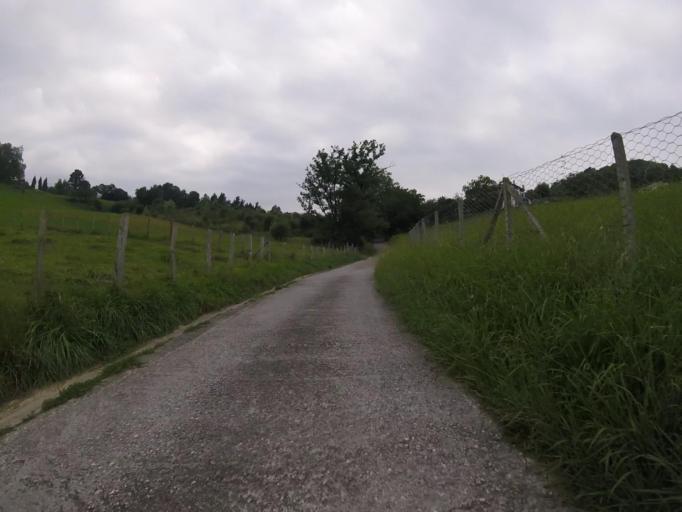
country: ES
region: Basque Country
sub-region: Provincia de Guipuzcoa
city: Lezo
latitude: 43.3094
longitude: -1.8405
